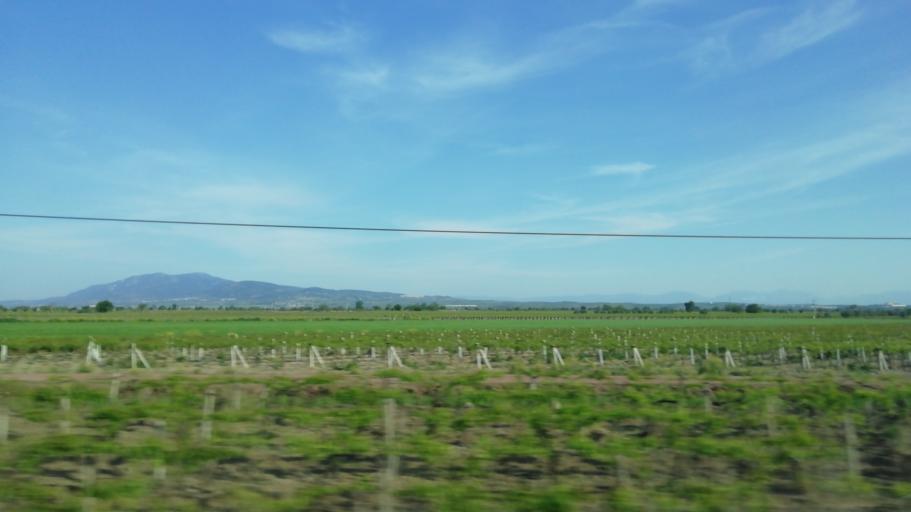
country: TR
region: Manisa
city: Saruhanli
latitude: 38.7354
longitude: 27.5919
